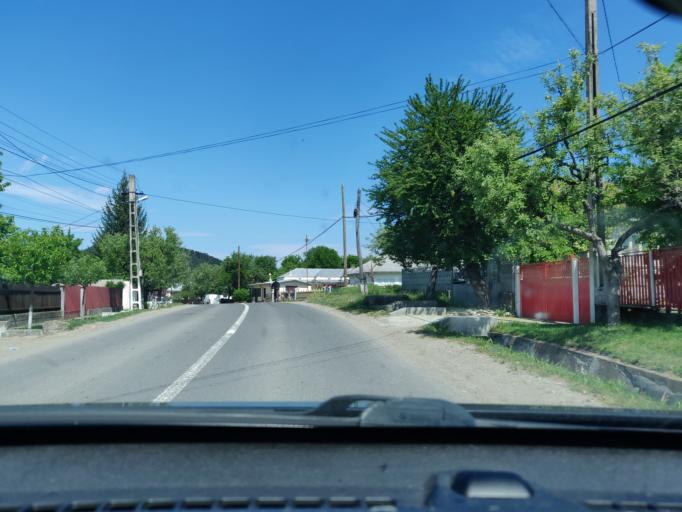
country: RO
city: Campurile de Jos
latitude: 46.0297
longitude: 26.7593
